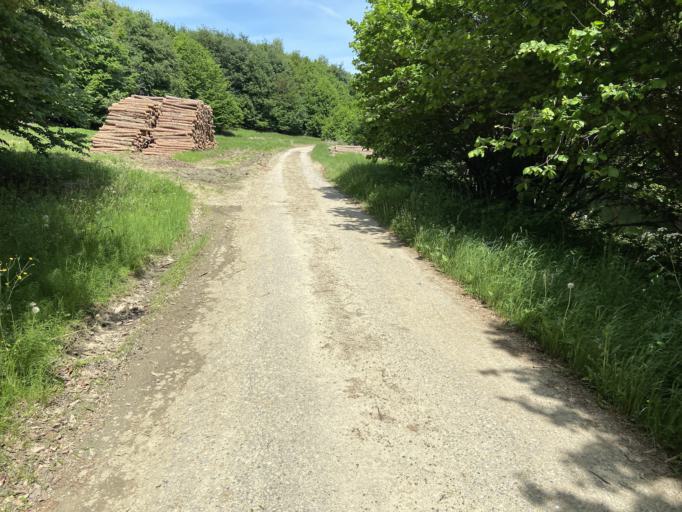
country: HU
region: Zala
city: Nagykanizsa
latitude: 46.5110
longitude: 16.8834
